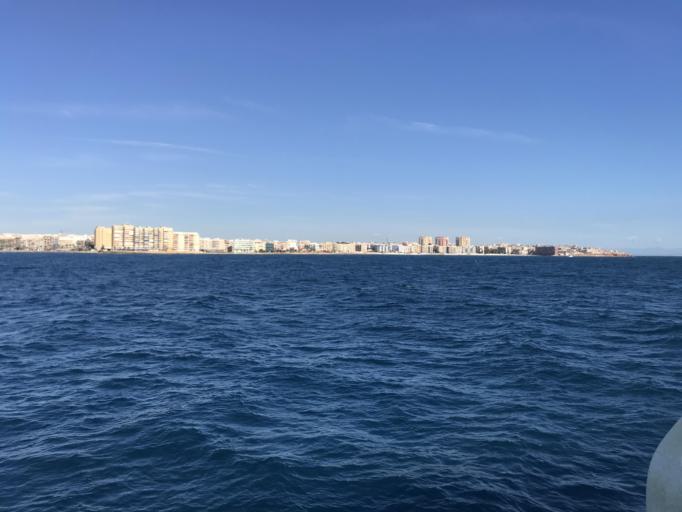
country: ES
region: Valencia
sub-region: Provincia de Alicante
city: Torrevieja
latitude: 37.9694
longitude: -0.6615
